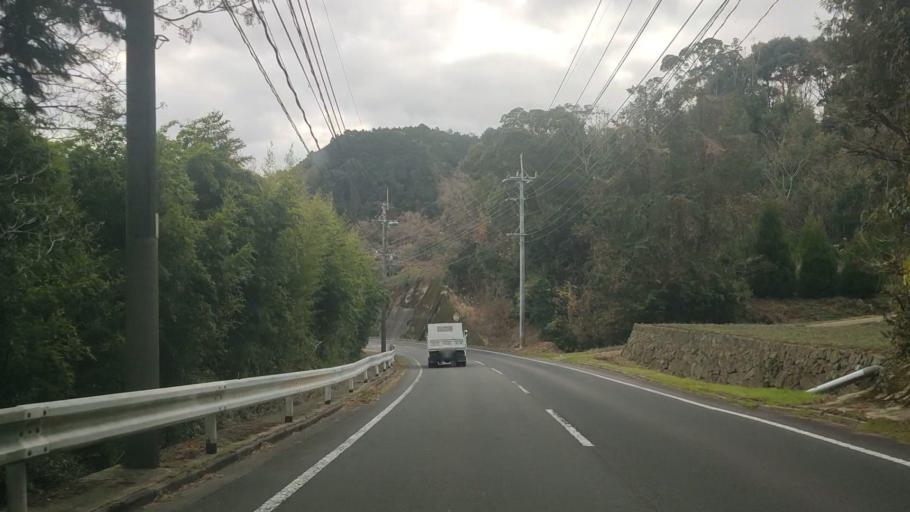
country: JP
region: Nagasaki
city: Shimabara
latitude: 32.8509
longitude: 130.2754
